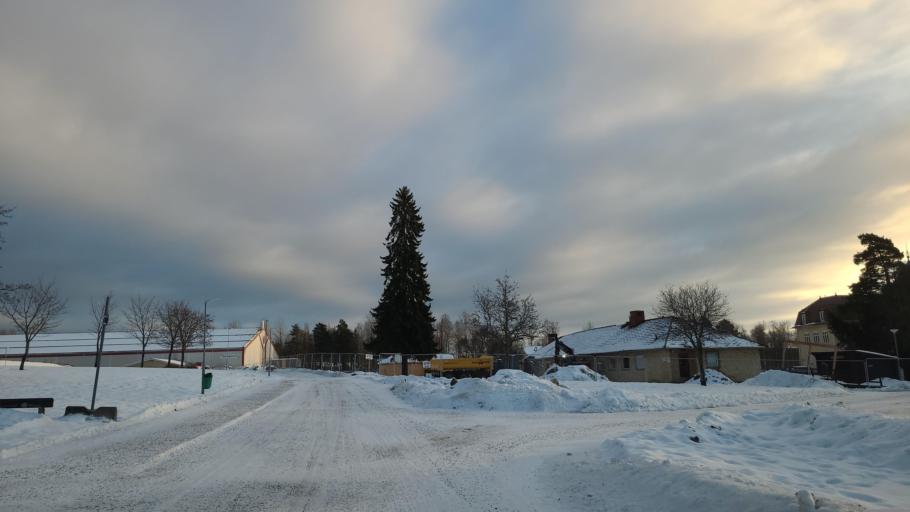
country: SE
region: Gaevleborg
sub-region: Bollnas Kommun
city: Bollnas
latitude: 61.3588
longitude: 16.4235
